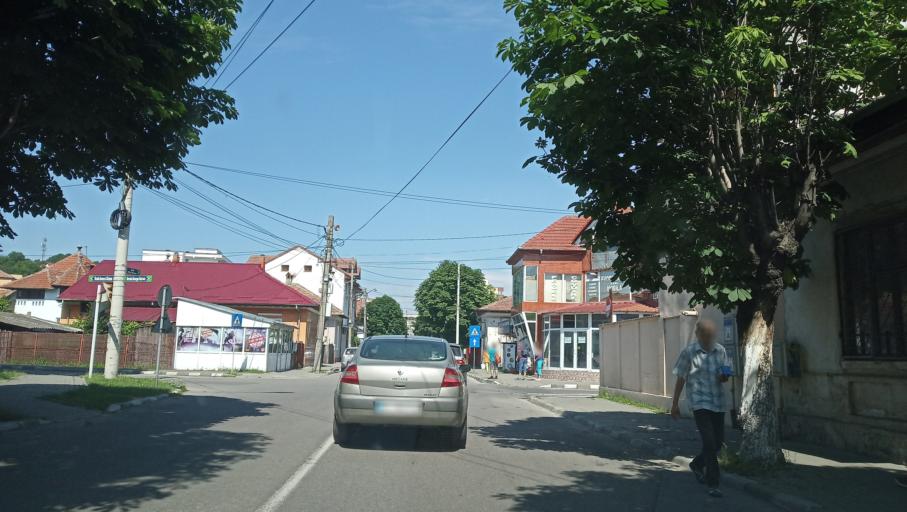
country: RO
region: Valcea
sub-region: Municipiul Ramnicu Valcea
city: Ramnicu Valcea
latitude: 45.0950
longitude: 24.3652
